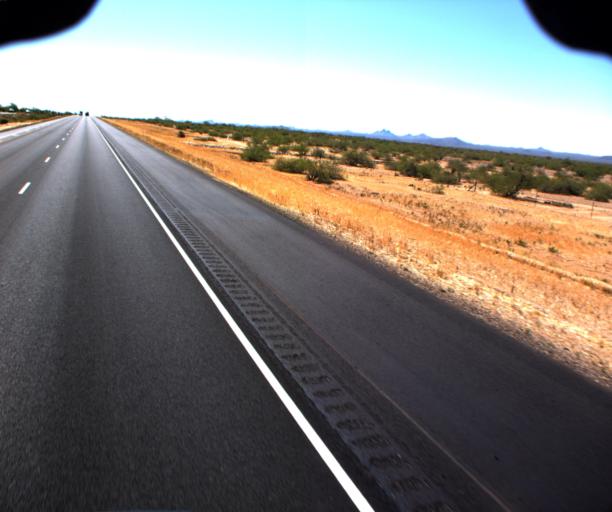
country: US
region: Arizona
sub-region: Yavapai County
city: Congress
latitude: 34.0900
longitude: -112.9031
